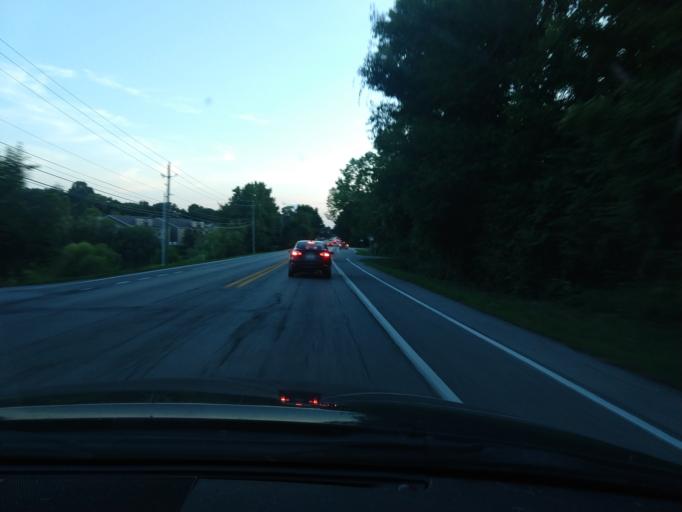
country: US
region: Indiana
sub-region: Marion County
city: Broad Ripple
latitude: 39.8574
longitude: -86.1026
